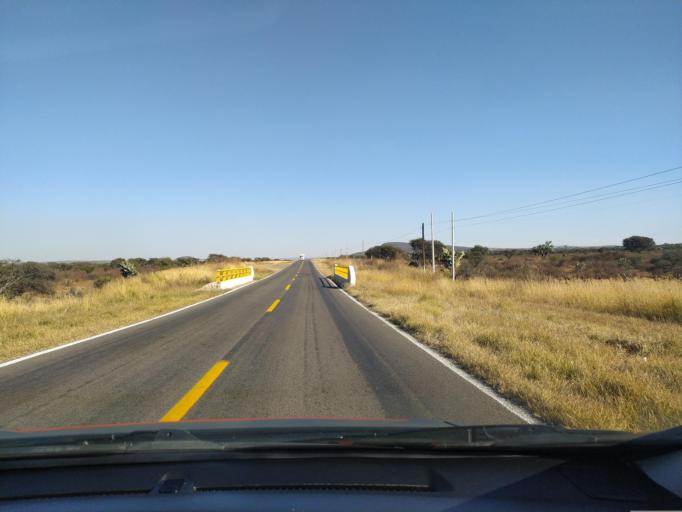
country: MX
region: Jalisco
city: San Miguel el Alto
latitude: 21.0178
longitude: -102.5005
